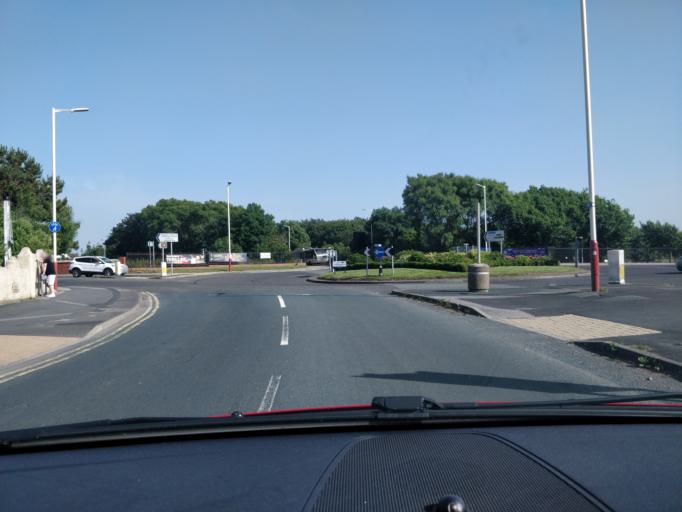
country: GB
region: England
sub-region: Sefton
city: Southport
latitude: 53.6473
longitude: -3.0200
